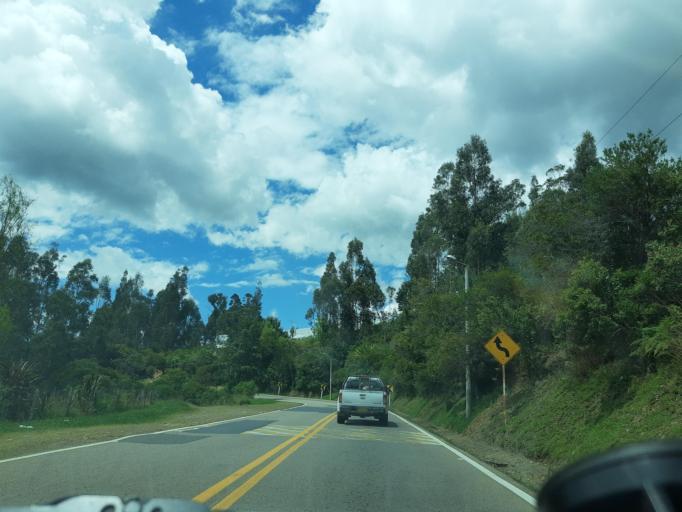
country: CO
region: Boyaca
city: Raquira
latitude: 5.5776
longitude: -73.6854
